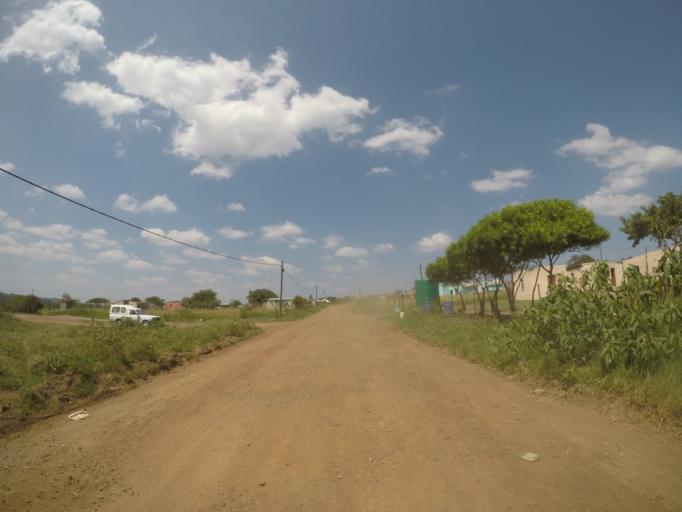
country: ZA
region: KwaZulu-Natal
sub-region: uThungulu District Municipality
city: Empangeni
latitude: -28.5885
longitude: 31.7381
